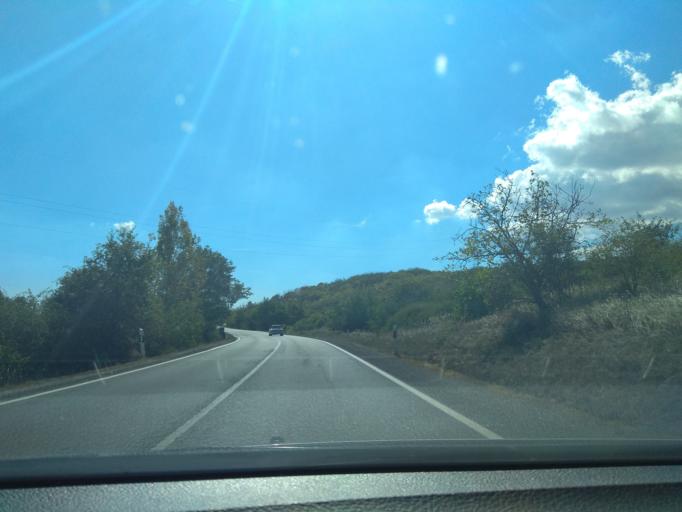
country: HU
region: Borsod-Abauj-Zemplen
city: Sarospatak
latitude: 48.3254
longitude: 21.5408
